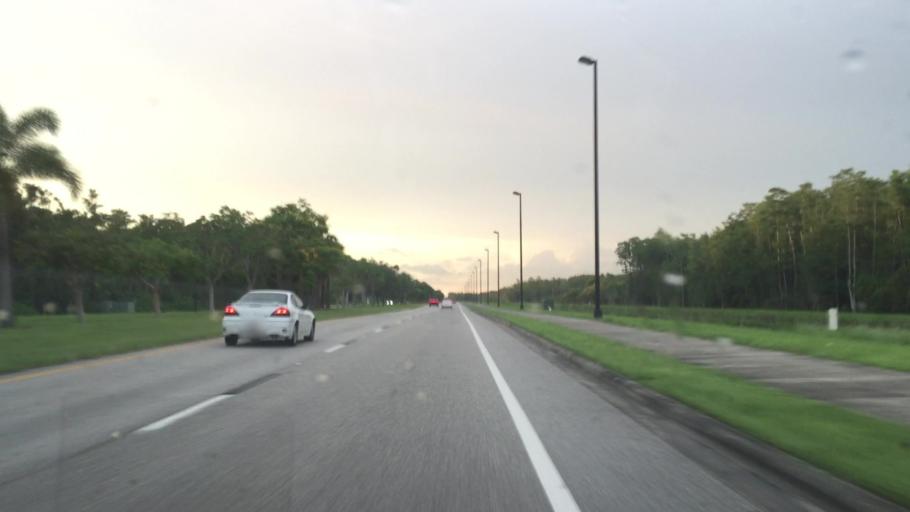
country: US
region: Florida
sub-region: Lee County
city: Three Oaks
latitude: 26.5185
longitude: -81.7854
